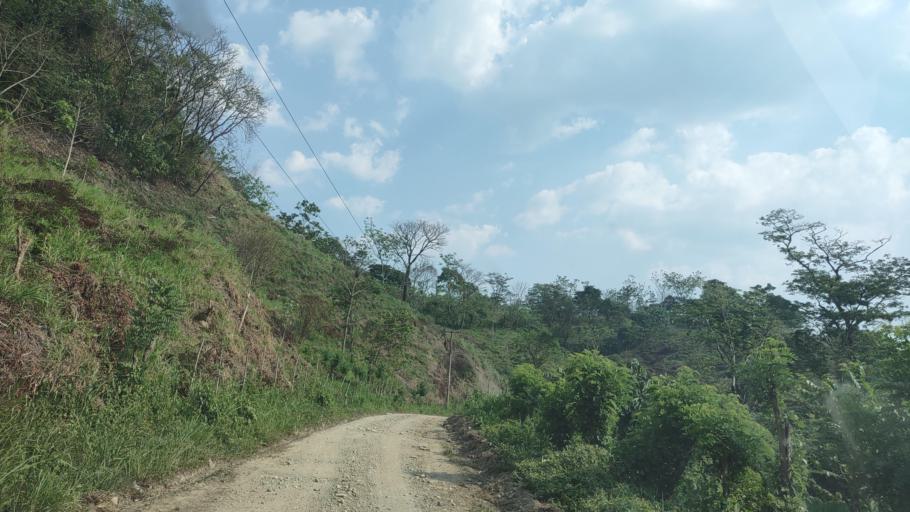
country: MX
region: Chiapas
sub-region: Tecpatan
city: Raudales Malpaso
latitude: 17.3188
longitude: -93.7410
